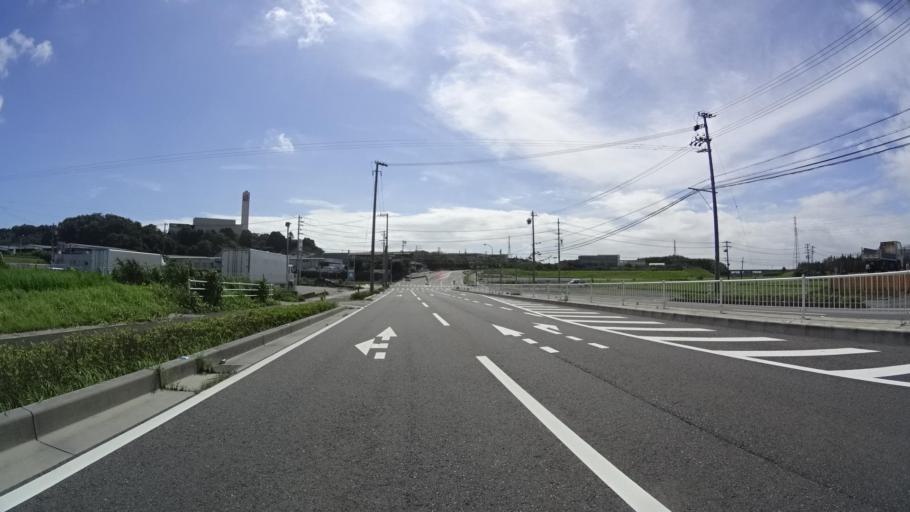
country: JP
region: Mie
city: Kawage
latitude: 34.8378
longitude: 136.5325
